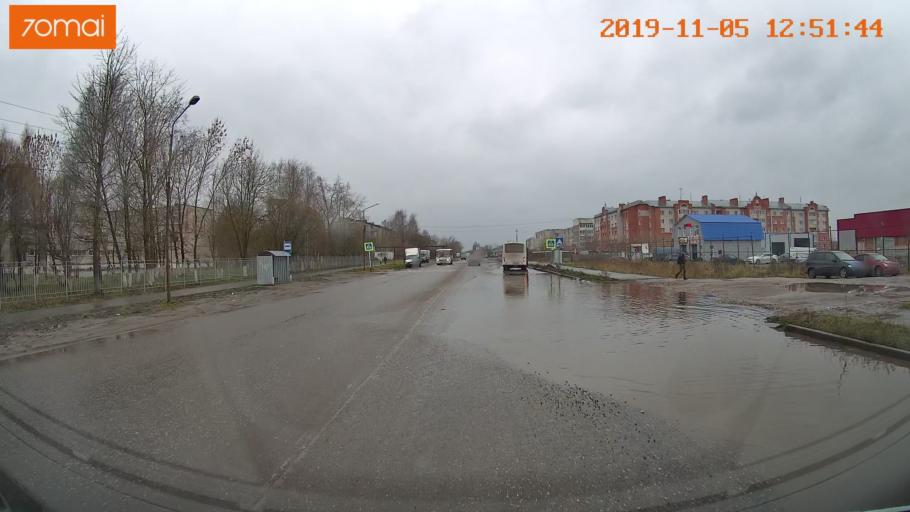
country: RU
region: Ivanovo
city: Kokhma
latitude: 56.9421
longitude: 41.1123
